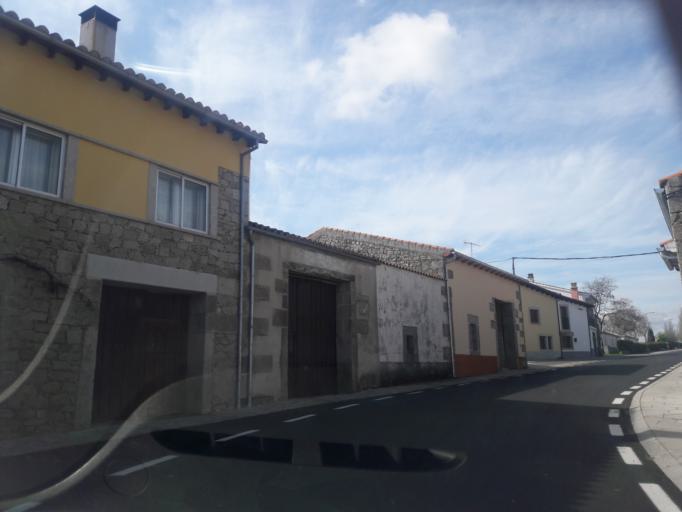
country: ES
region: Castille and Leon
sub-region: Provincia de Salamanca
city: Endrinal
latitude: 40.5431
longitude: -5.8005
